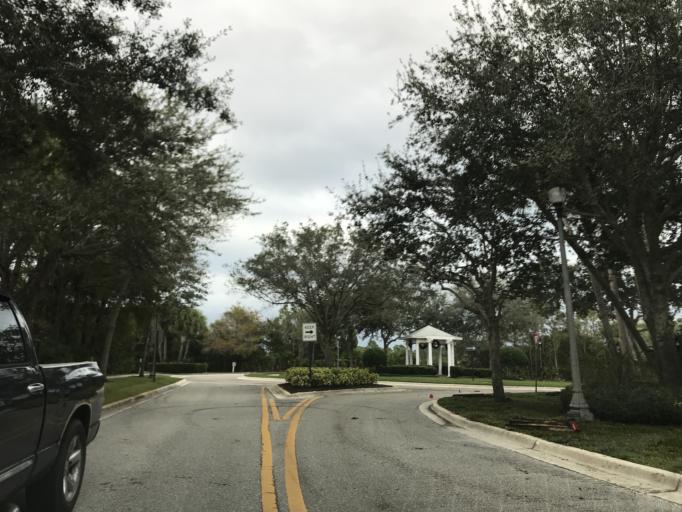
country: US
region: Florida
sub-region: Palm Beach County
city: Jupiter
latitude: 26.9166
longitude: -80.1000
